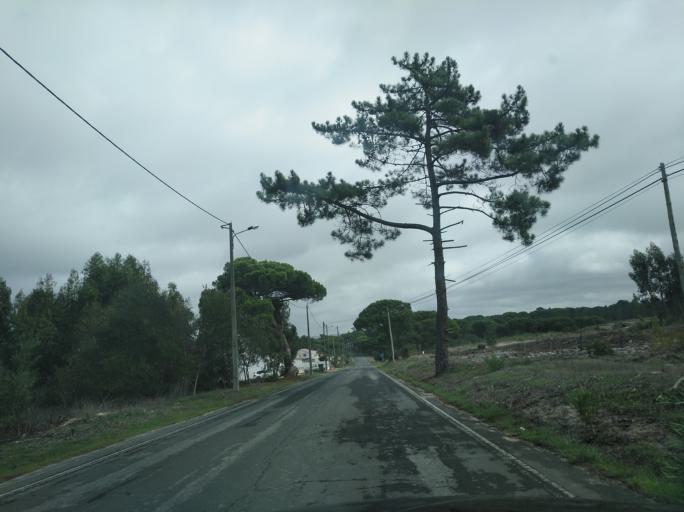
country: PT
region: Setubal
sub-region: Santiago do Cacem
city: Santo Andre
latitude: 38.1314
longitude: -8.7790
